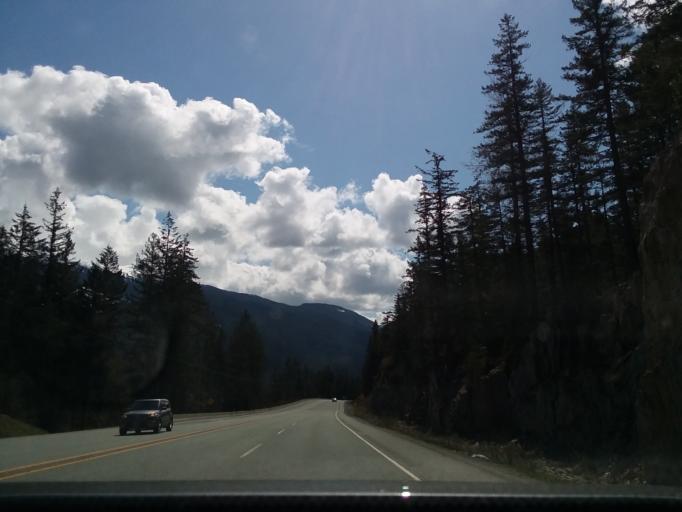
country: CA
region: British Columbia
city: Whistler
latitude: 50.0313
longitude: -123.1223
